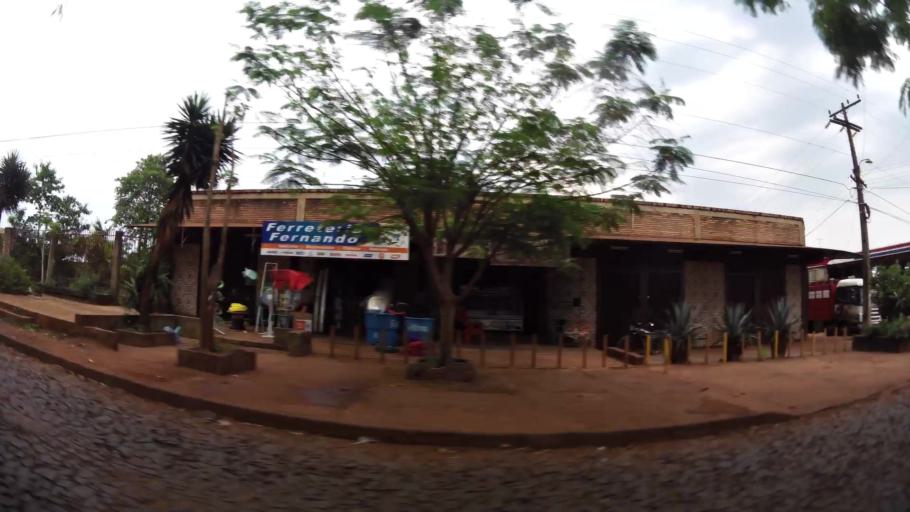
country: PY
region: Alto Parana
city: Presidente Franco
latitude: -25.5361
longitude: -54.6499
